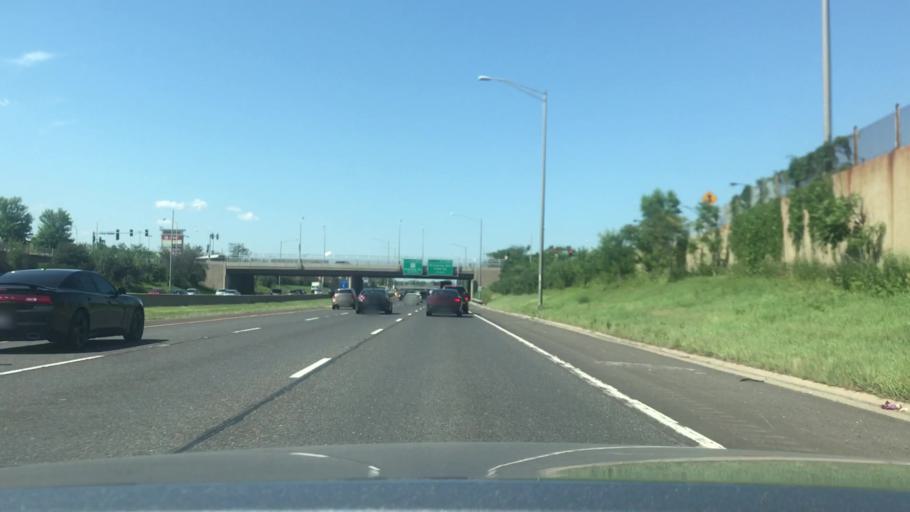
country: US
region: Illinois
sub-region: Cook County
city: Calumet Park
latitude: 41.6759
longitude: -87.6617
